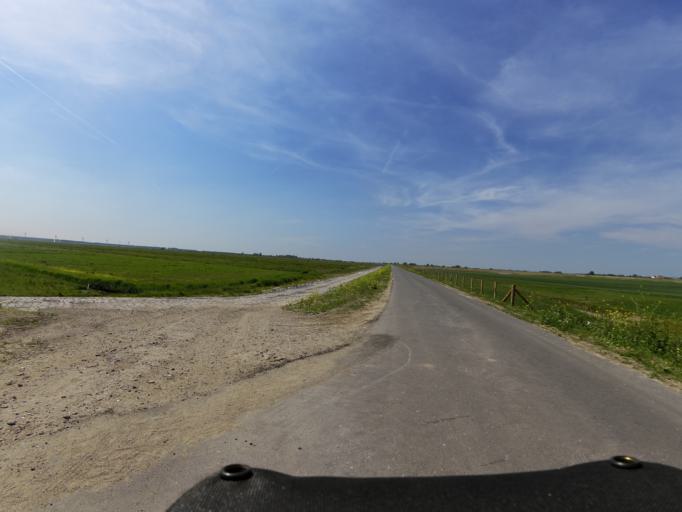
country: NL
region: South Holland
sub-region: Gemeente Spijkenisse
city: Spijkenisse
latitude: 51.7754
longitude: 4.2653
